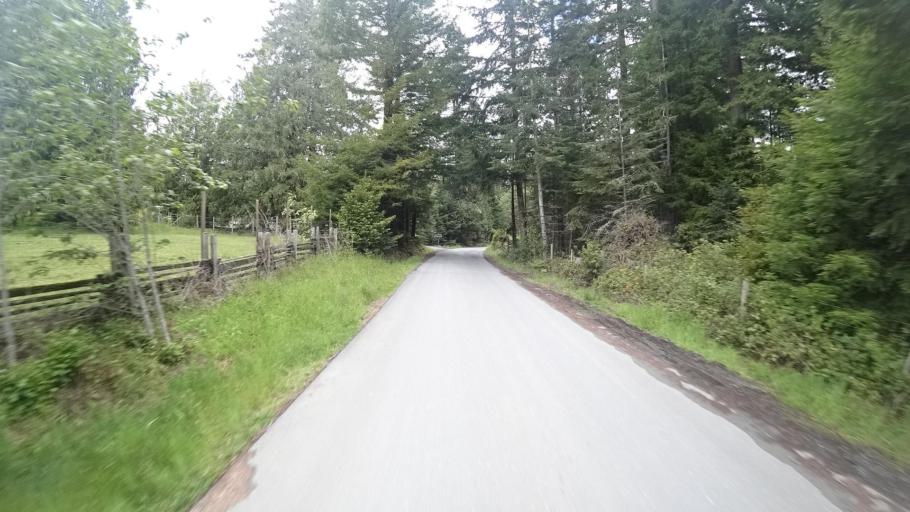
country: US
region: California
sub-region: Humboldt County
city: Blue Lake
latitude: 40.9078
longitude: -123.9732
